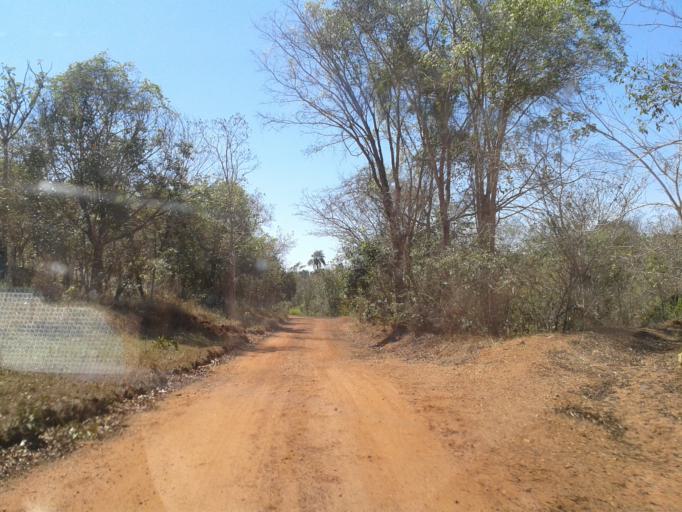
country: BR
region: Minas Gerais
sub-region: Monte Alegre De Minas
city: Monte Alegre de Minas
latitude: -18.8273
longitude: -49.1185
